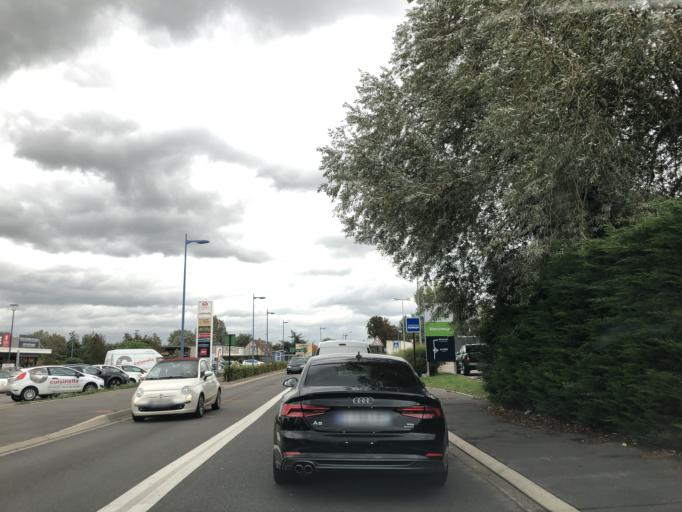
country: FR
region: Nord-Pas-de-Calais
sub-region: Departement du Pas-de-Calais
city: Merlimont
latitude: 50.4522
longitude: 1.6145
